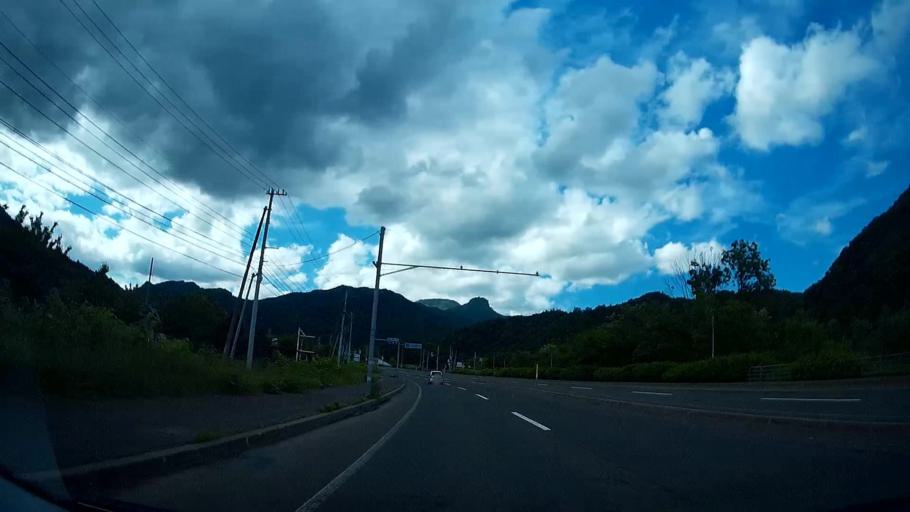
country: JP
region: Hokkaido
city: Sapporo
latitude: 42.9641
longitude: 141.2212
